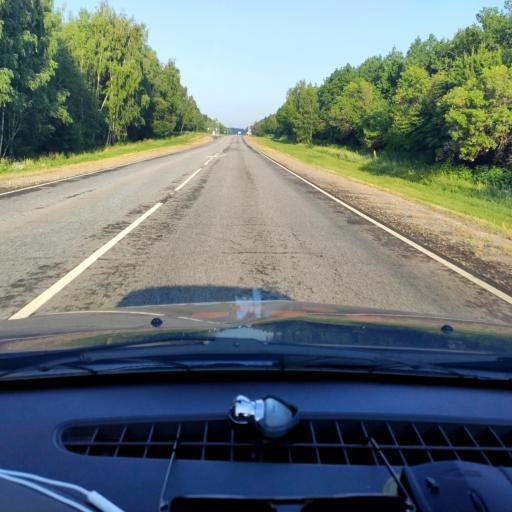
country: RU
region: Lipetsk
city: Izmalkovo
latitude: 52.4387
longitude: 37.9336
